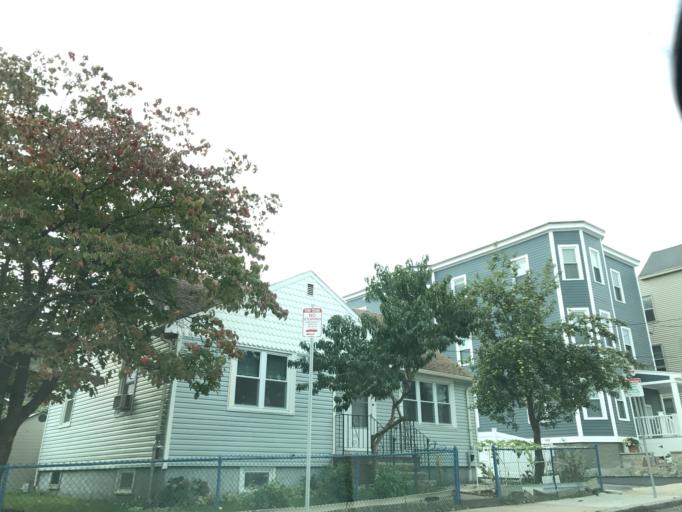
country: US
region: Massachusetts
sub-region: Suffolk County
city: South Boston
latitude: 42.3171
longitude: -71.0526
